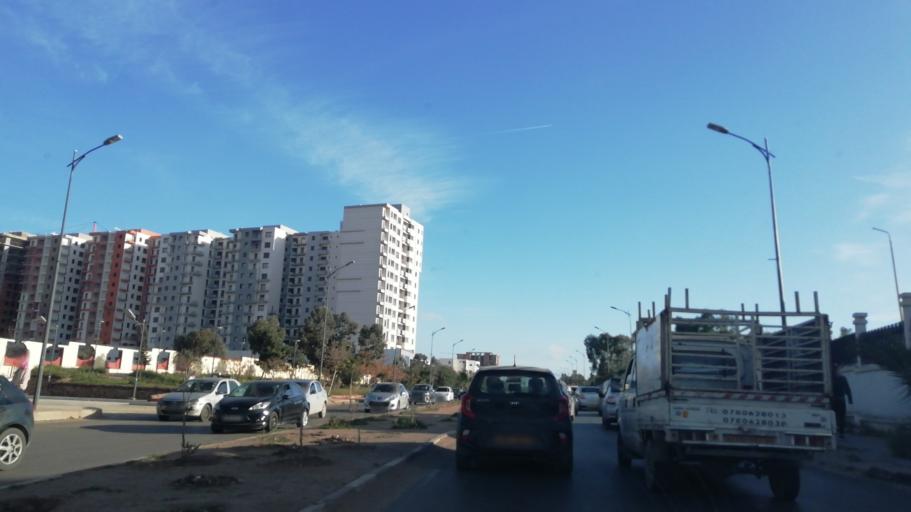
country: DZ
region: Oran
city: Bir el Djir
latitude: 35.7136
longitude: -0.5770
